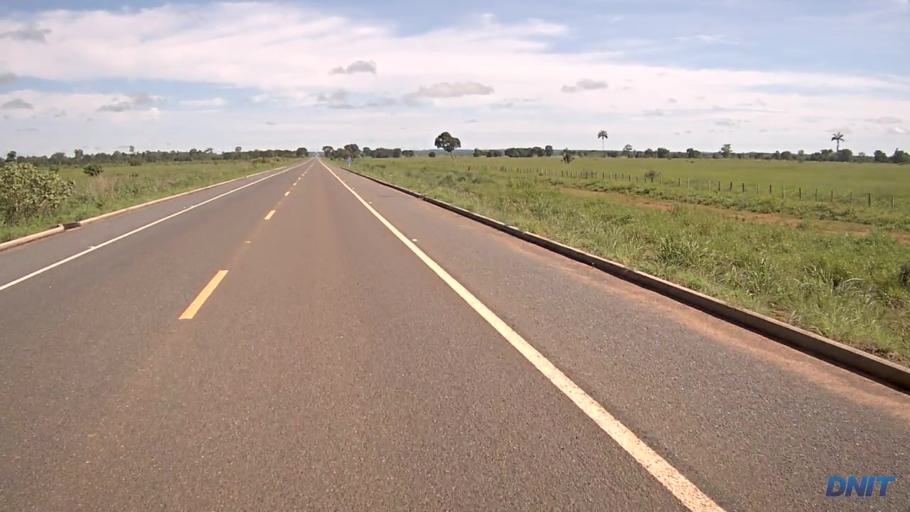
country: BR
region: Goias
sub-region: Sao Miguel Do Araguaia
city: Sao Miguel do Araguaia
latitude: -13.4261
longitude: -50.1277
